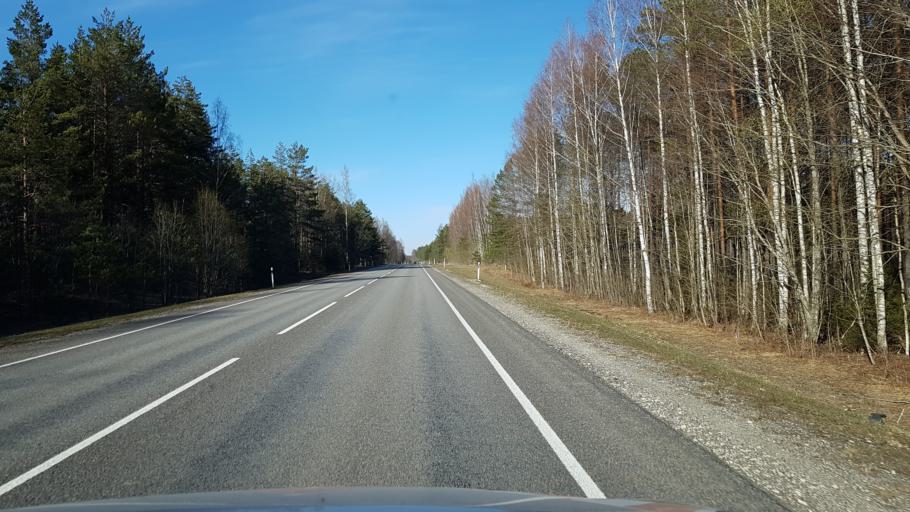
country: EE
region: Ida-Virumaa
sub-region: Kohtla-Nomme vald
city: Kohtla-Nomme
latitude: 59.0288
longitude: 27.2337
